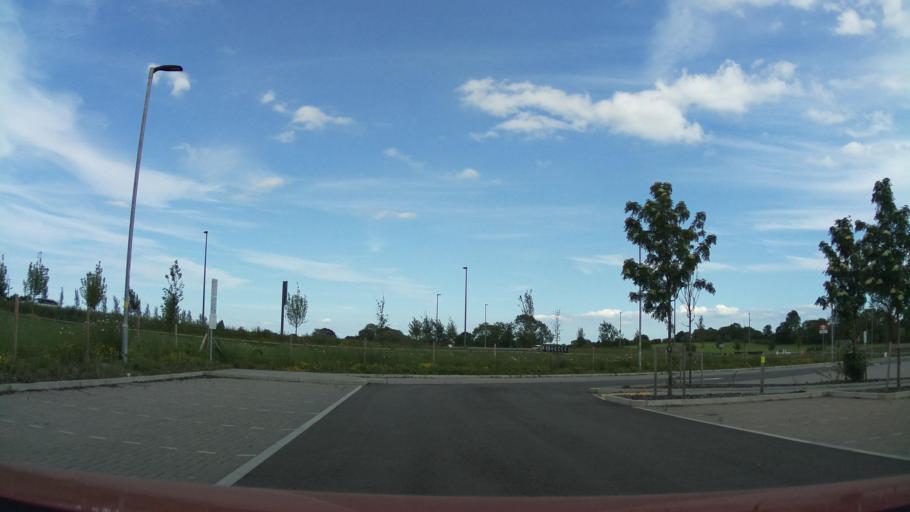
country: GB
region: England
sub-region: Worcestershire
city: Kempsey
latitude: 52.1579
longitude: -2.1579
